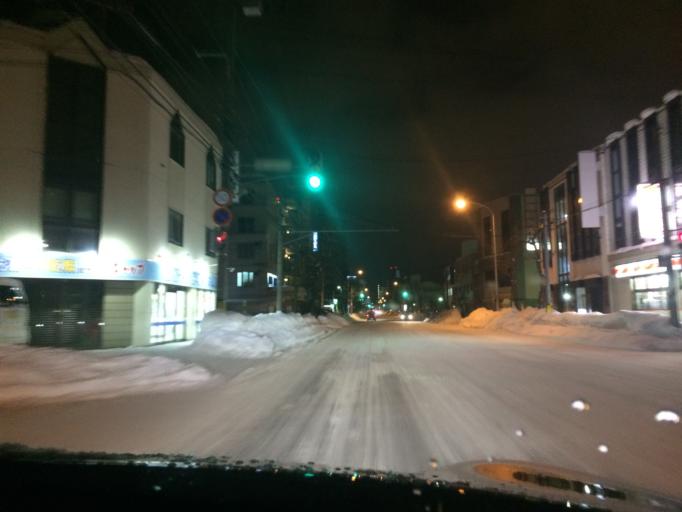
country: JP
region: Hokkaido
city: Sapporo
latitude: 43.0608
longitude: 141.3756
